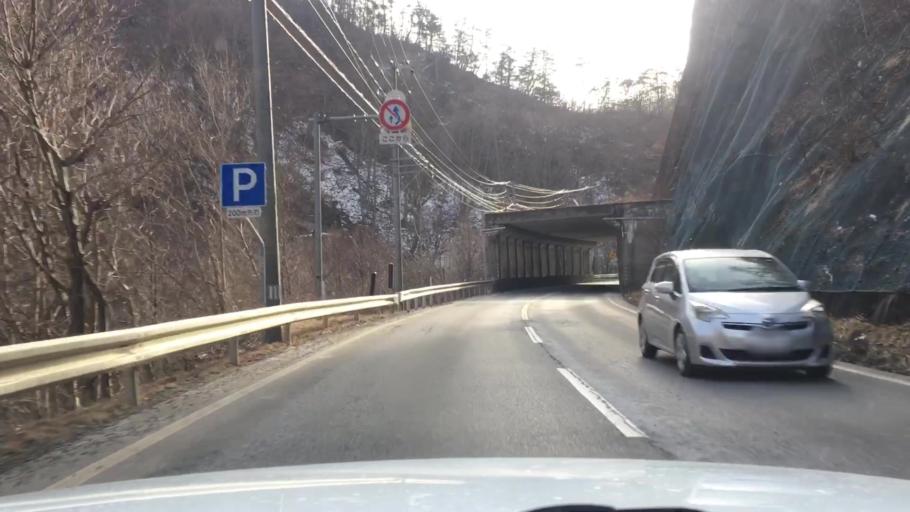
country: JP
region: Iwate
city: Tono
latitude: 39.6354
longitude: 141.5368
